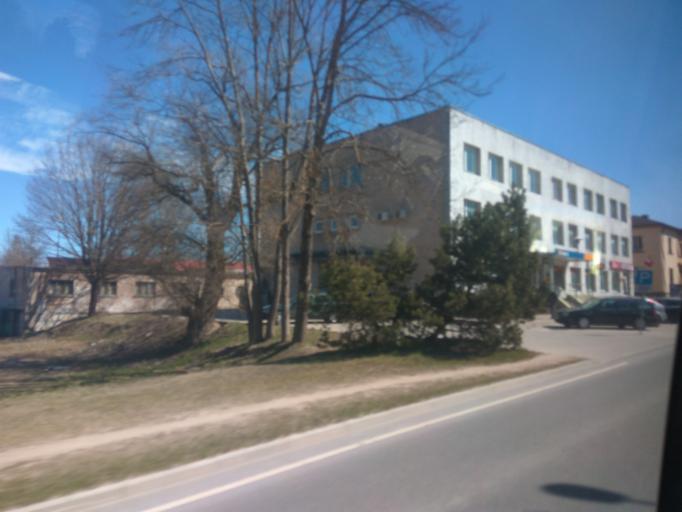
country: LV
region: Aluksnes Rajons
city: Aluksne
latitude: 57.4250
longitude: 27.0451
